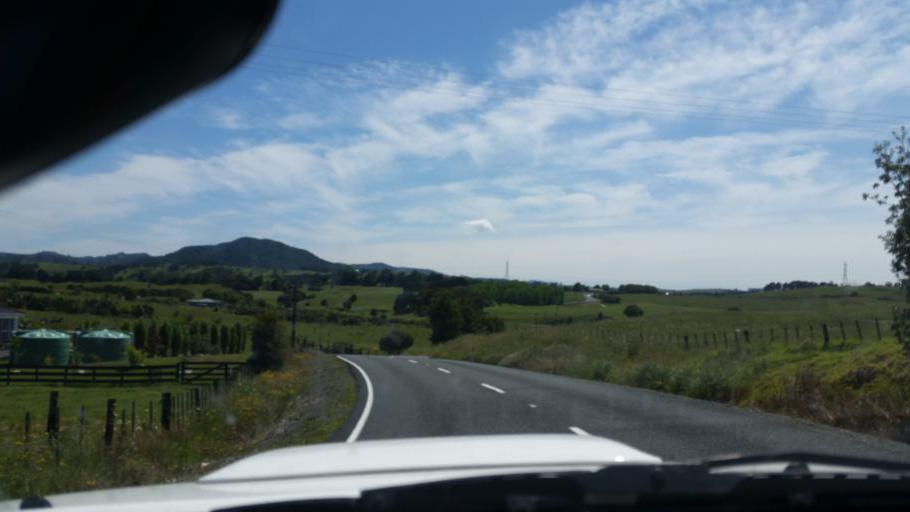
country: NZ
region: Auckland
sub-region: Auckland
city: Wellsford
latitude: -36.1704
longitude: 174.4203
